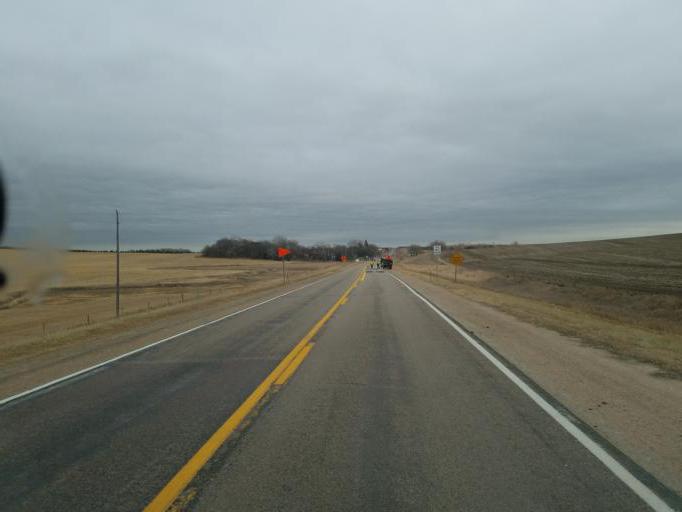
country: US
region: Nebraska
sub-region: Cedar County
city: Hartington
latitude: 42.6127
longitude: -97.4363
